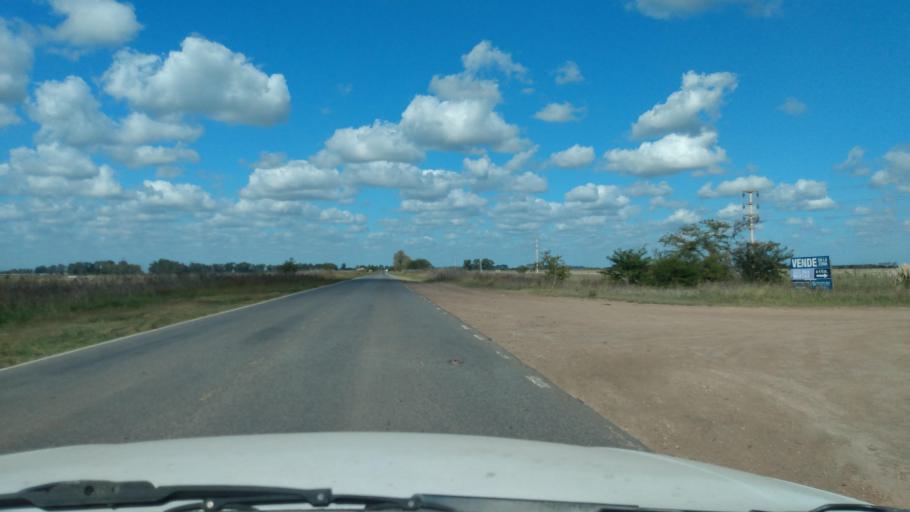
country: AR
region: Buenos Aires
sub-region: Partido de Navarro
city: Navarro
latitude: -34.8650
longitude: -59.3427
